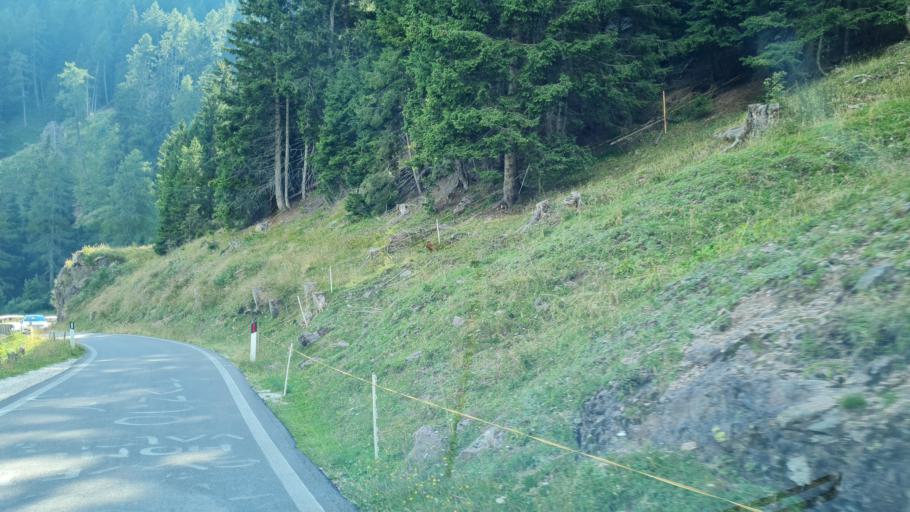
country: IT
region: Trentino-Alto Adige
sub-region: Provincia di Trento
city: Palu del Fersina
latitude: 46.1647
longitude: 11.4335
